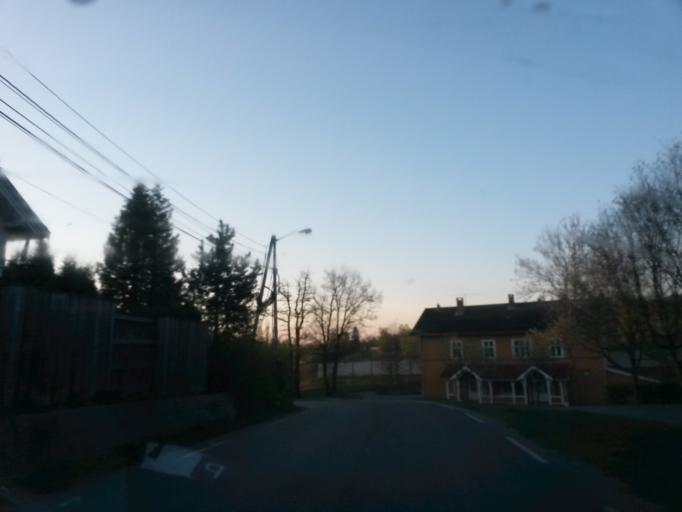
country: NO
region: Akershus
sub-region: Asker
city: Asker
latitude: 59.8294
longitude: 10.4038
